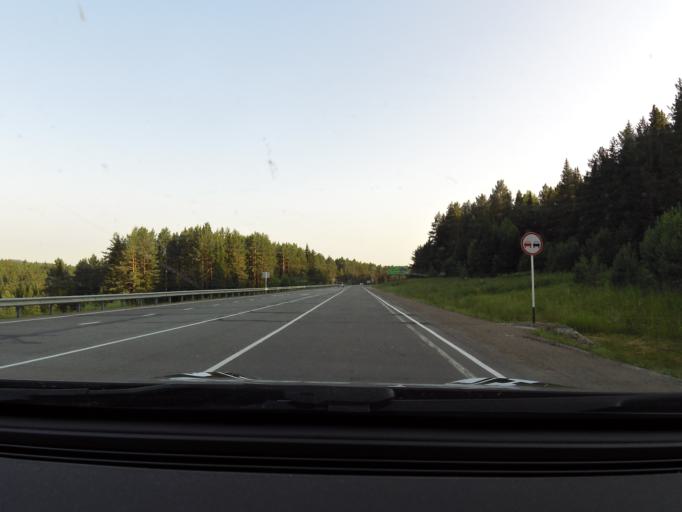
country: RU
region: Sverdlovsk
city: Nizhniye Sergi
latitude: 56.6404
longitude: 59.2480
